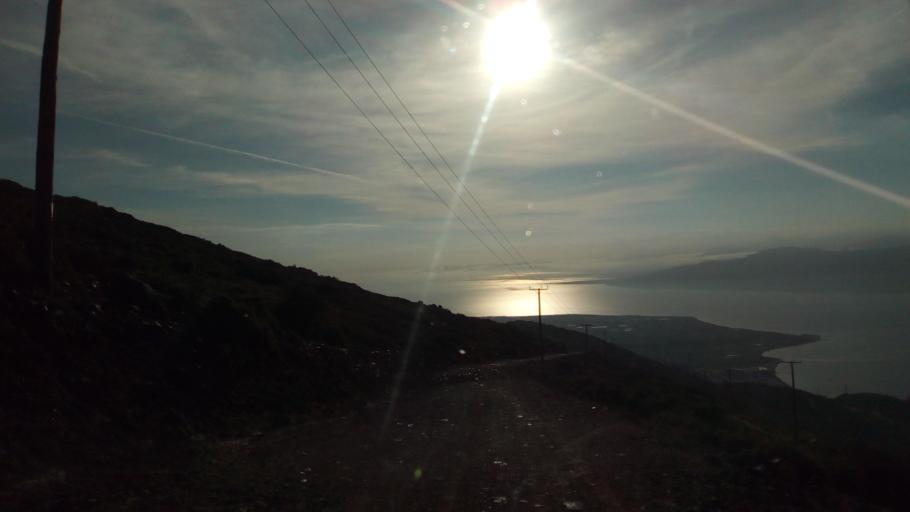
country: GR
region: West Greece
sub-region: Nomos Aitolias kai Akarnanias
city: Nafpaktos
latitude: 38.4184
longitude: 21.8073
